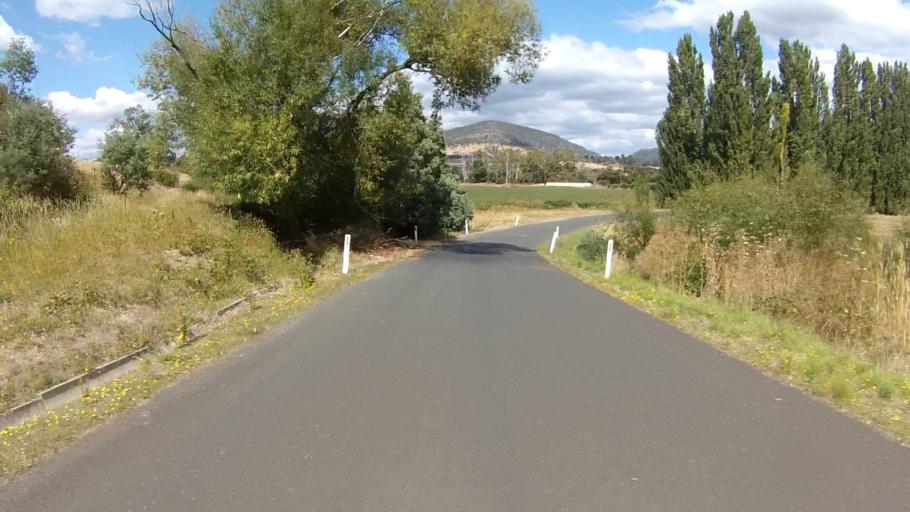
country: AU
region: Tasmania
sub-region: Derwent Valley
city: New Norfolk
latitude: -42.7521
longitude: 146.9720
